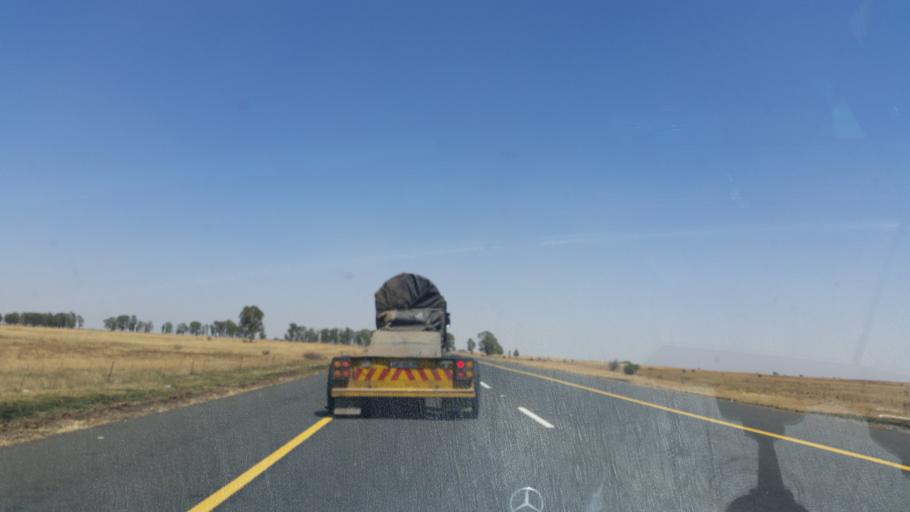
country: ZA
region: Orange Free State
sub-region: Lejweleputswa District Municipality
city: Winburg
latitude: -28.6377
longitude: 26.8946
